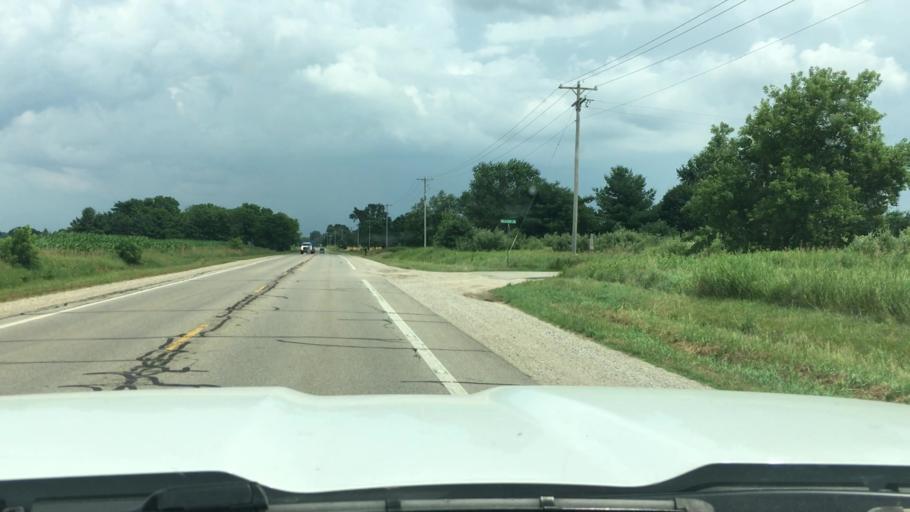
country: US
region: Michigan
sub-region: Montcalm County
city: Greenville
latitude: 43.1703
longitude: -85.1980
